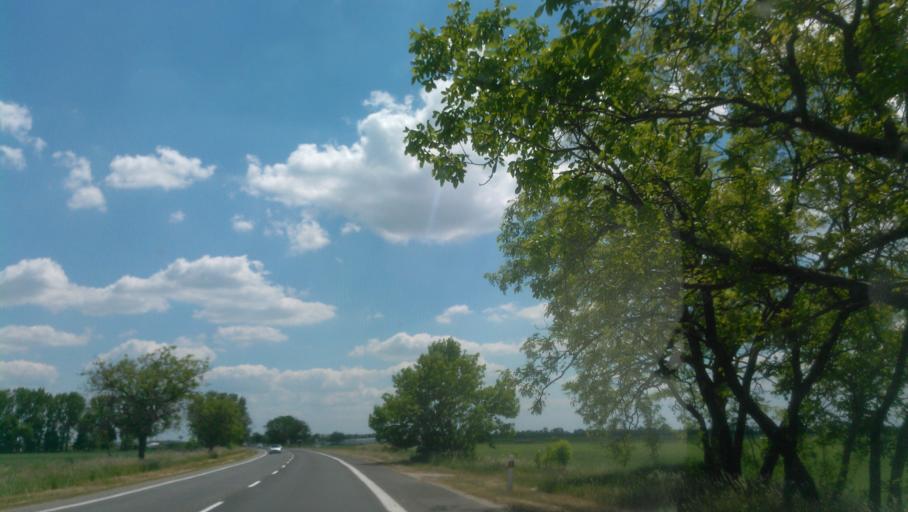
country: SK
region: Bratislavsky
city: Dunajska Luzna
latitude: 48.0586
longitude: 17.2838
